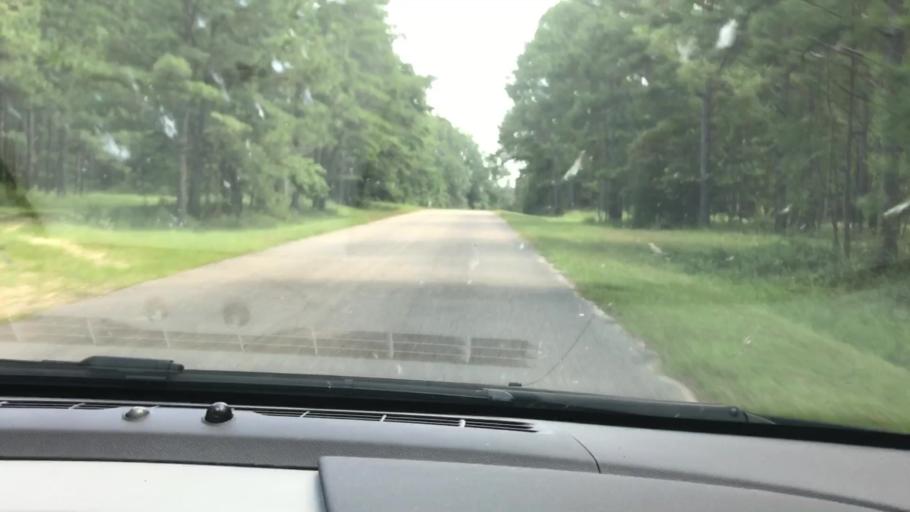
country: US
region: Georgia
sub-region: Clay County
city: Fort Gaines
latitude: 31.7423
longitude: -85.0766
